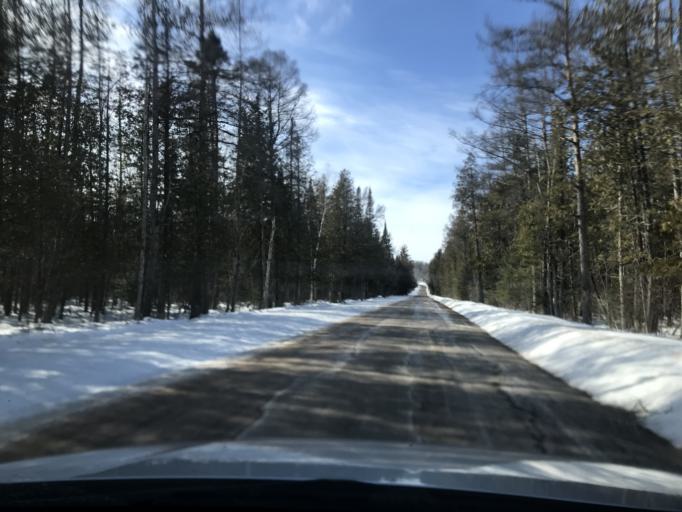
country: US
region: Wisconsin
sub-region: Marinette County
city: Peshtigo
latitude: 45.3007
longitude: -87.8286
